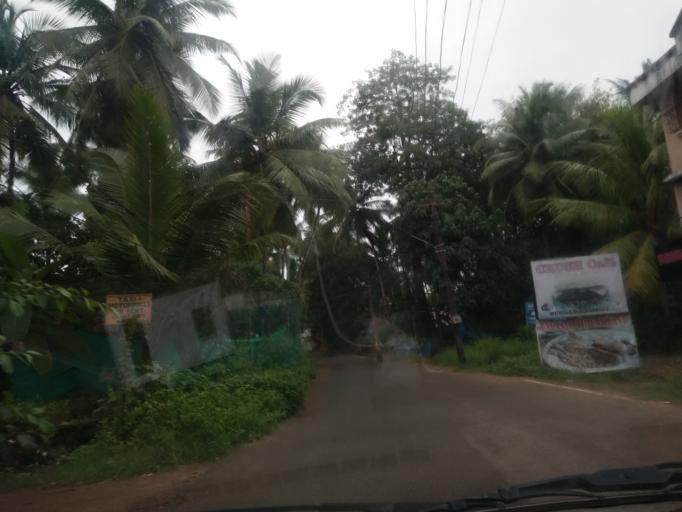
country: IN
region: Goa
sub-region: South Goa
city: Benaulim
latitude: 15.2607
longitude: 73.9285
